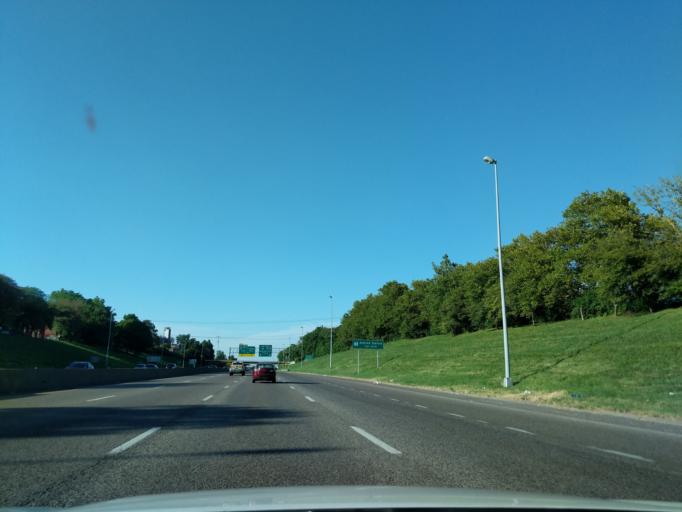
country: US
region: Missouri
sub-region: City of Saint Louis
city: St. Louis
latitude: 38.5988
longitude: -90.2155
